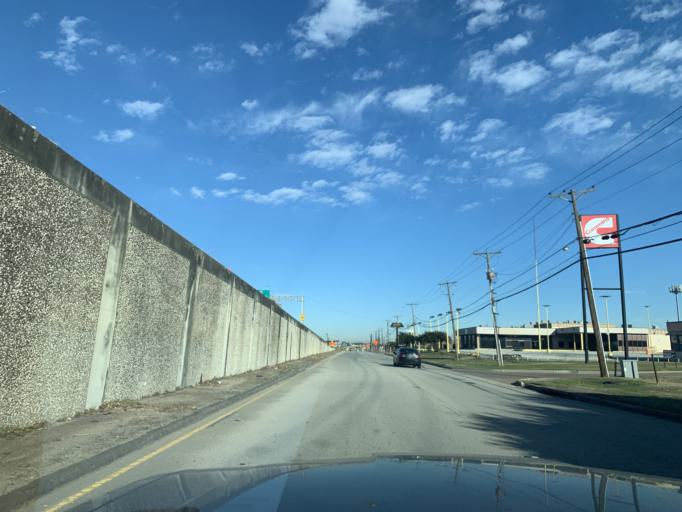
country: US
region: Texas
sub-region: Tarrant County
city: Arlington
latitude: 32.7502
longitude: -97.0624
